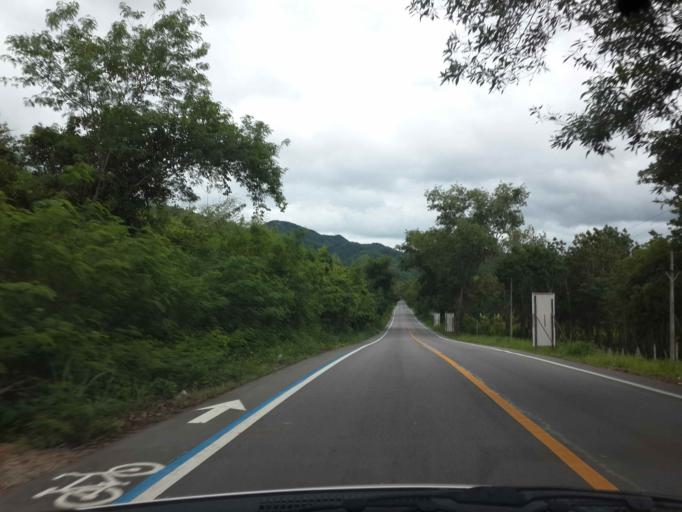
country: TH
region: Ratchaburi
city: Suan Phueng
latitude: 13.5963
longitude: 99.2350
